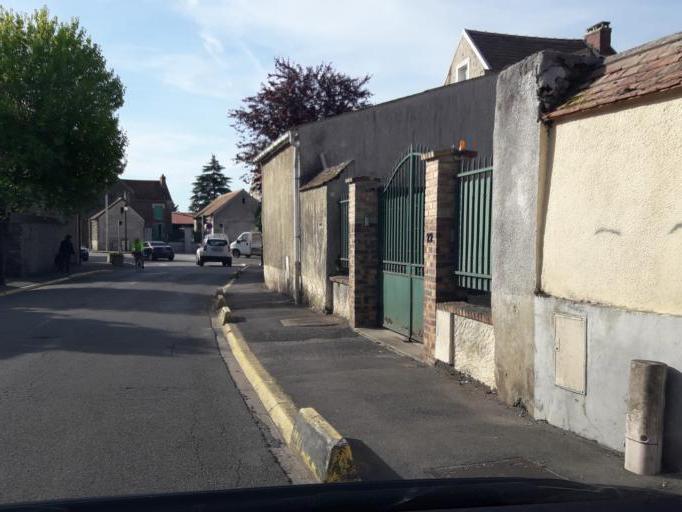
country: FR
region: Ile-de-France
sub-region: Departement de l'Essonne
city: Leudeville
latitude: 48.5655
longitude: 2.3275
